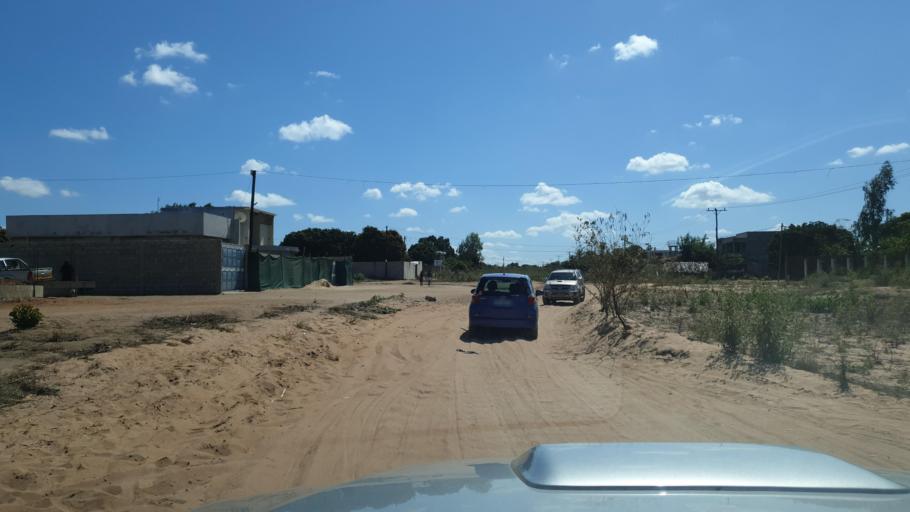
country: MZ
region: Nampula
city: Nampula
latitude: -15.1072
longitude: 39.2061
